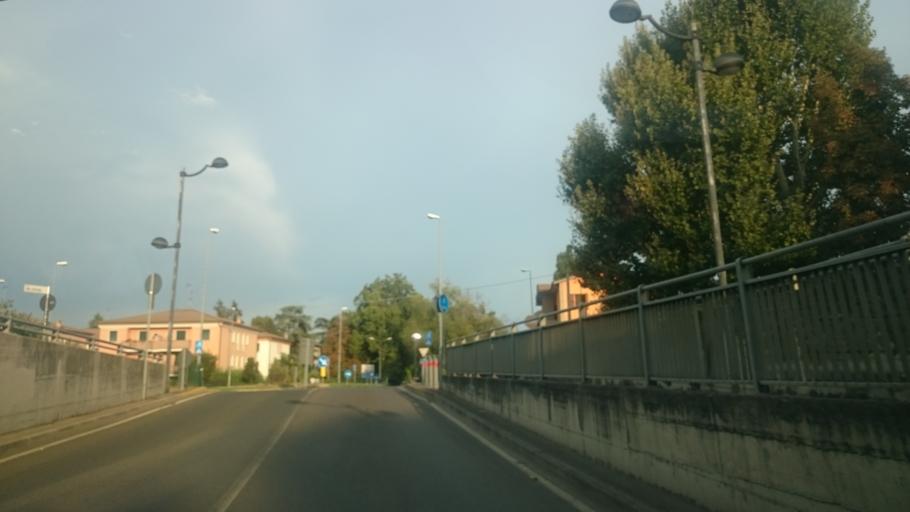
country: IT
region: Emilia-Romagna
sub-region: Provincia di Reggio Emilia
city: Reggio nell'Emilia
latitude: 44.7099
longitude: 10.6451
